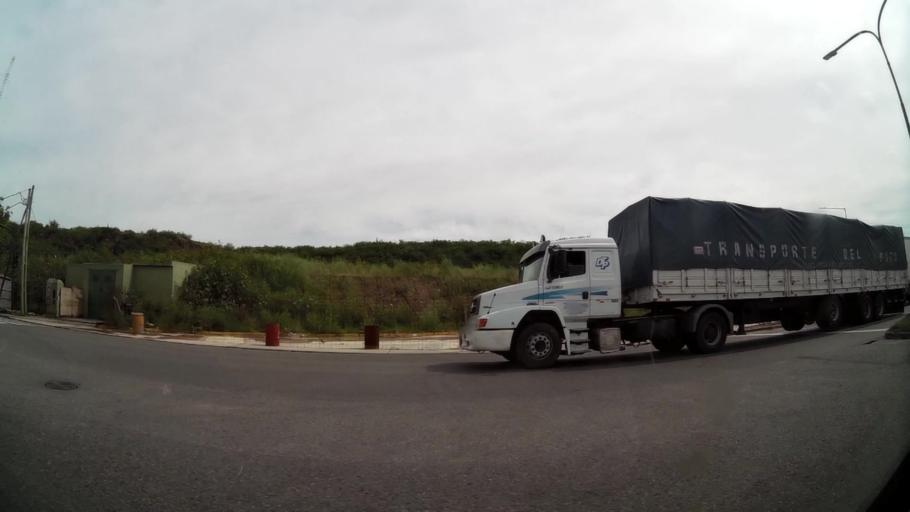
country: AR
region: Buenos Aires F.D.
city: Villa Lugano
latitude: -34.6687
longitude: -58.4356
